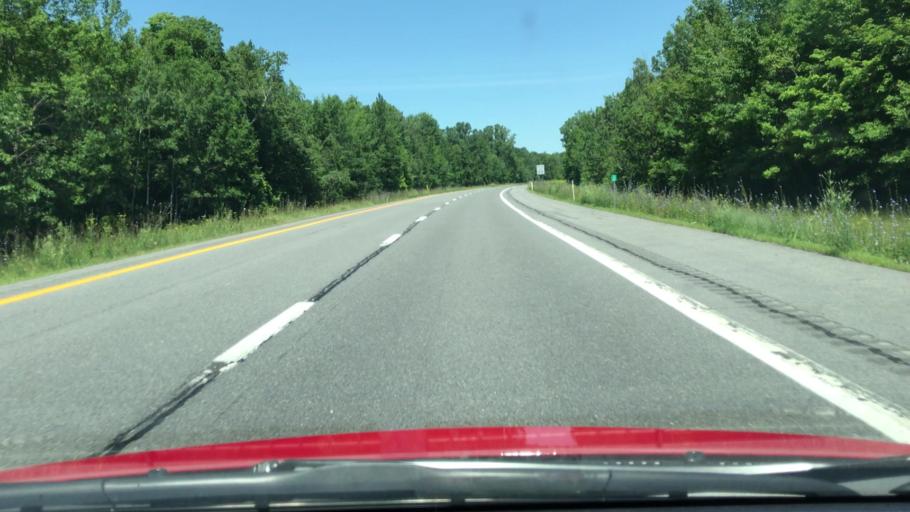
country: US
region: New York
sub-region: Clinton County
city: Champlain
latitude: 44.8992
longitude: -73.4545
